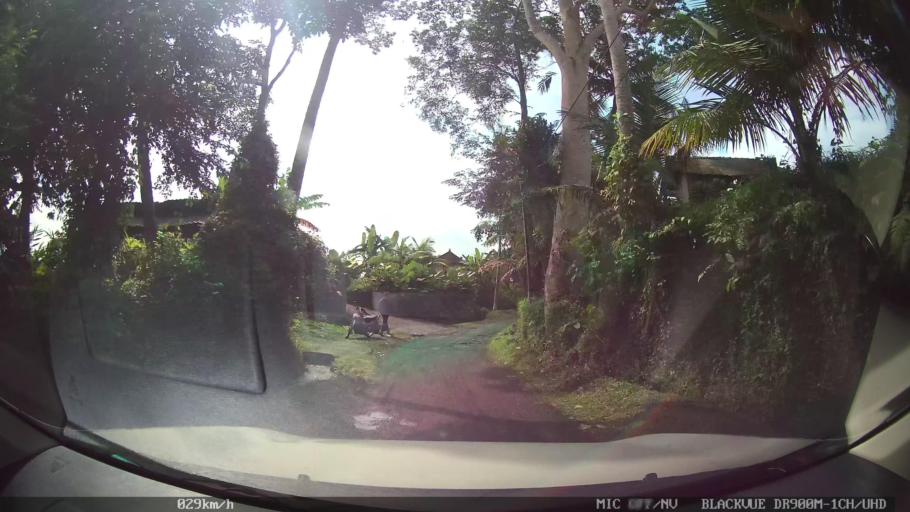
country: ID
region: Bali
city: Banjar Pesalakan
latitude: -8.5106
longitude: 115.3063
